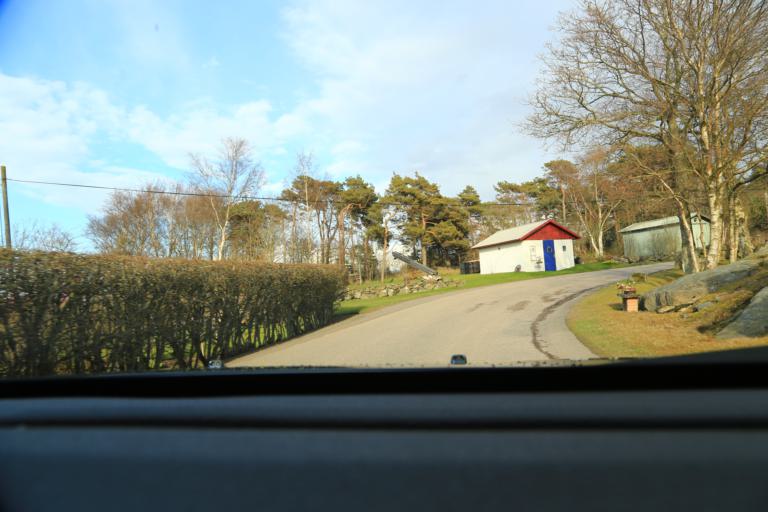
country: SE
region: Halland
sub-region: Varbergs Kommun
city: Traslovslage
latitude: 57.0509
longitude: 12.3046
